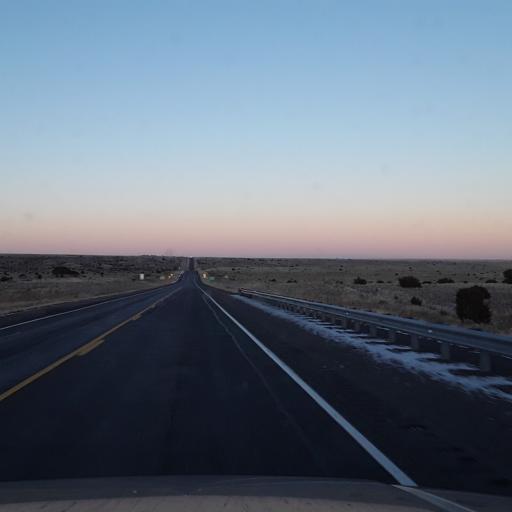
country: US
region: New Mexico
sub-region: Guadalupe County
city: Santa Rosa
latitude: 34.5351
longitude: -105.3155
